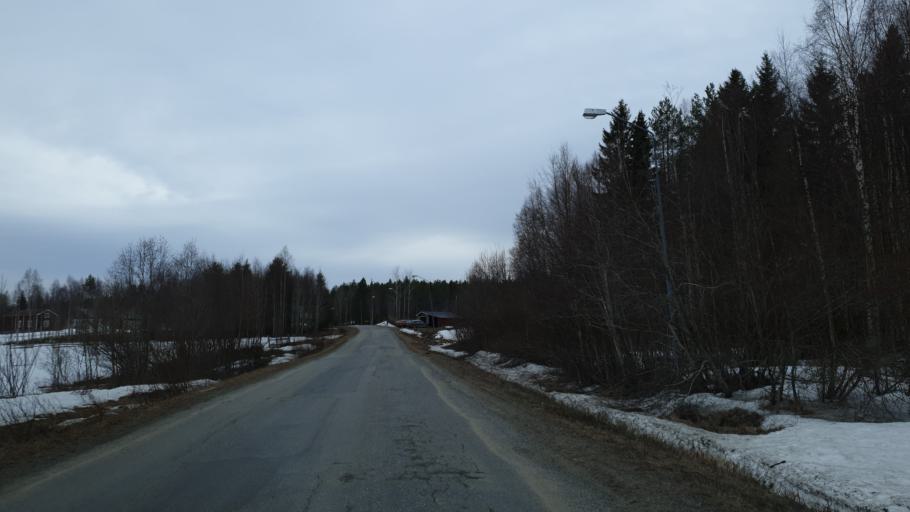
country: SE
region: Vaesterbotten
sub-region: Robertsfors Kommun
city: Robertsfors
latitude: 64.3970
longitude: 21.0028
